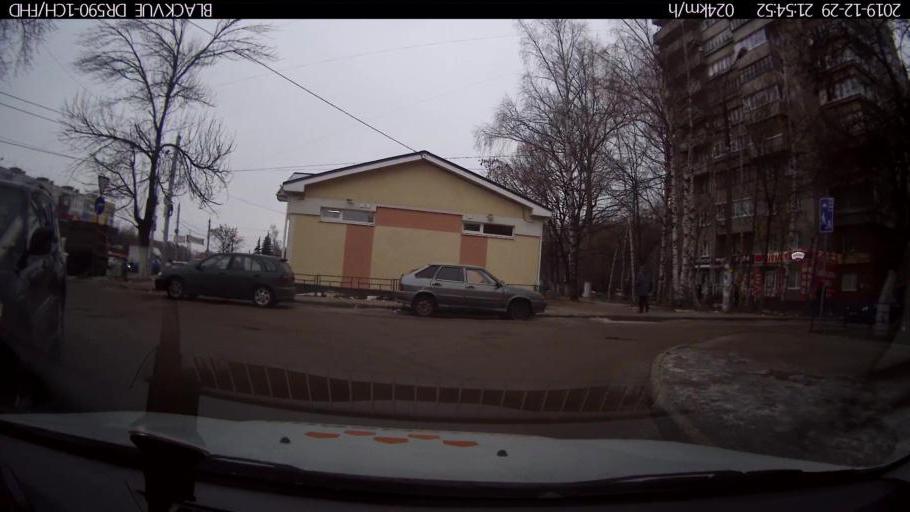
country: RU
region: Nizjnij Novgorod
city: Nizhniy Novgorod
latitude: 56.2326
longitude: 43.9462
